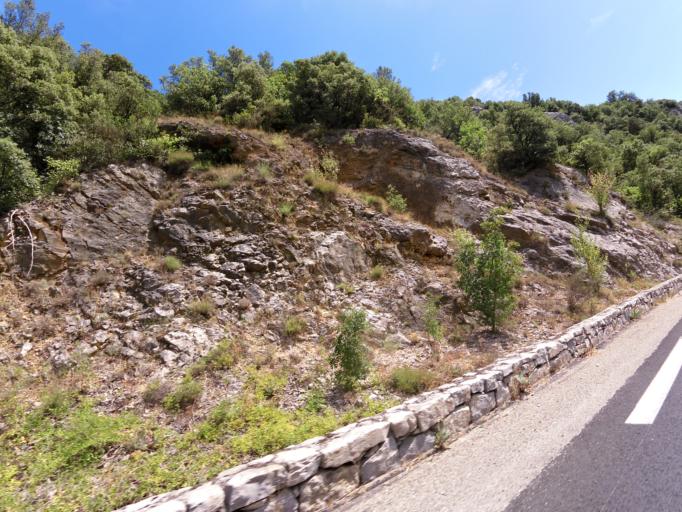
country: FR
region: Languedoc-Roussillon
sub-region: Departement de l'Herault
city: Ganges
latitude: 43.9406
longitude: 3.6904
